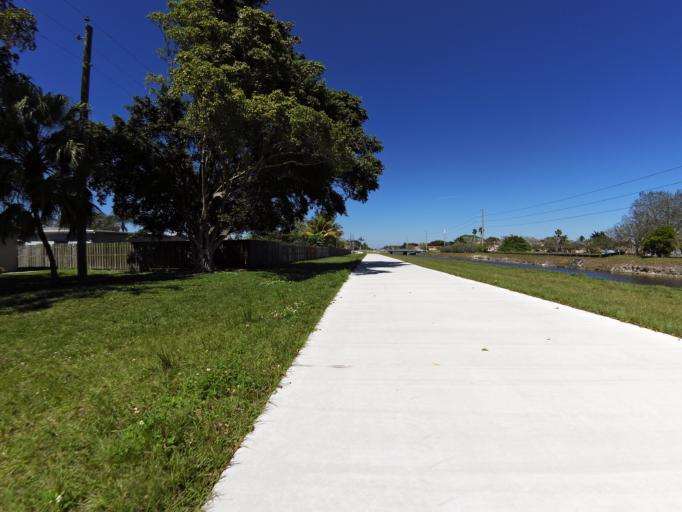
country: US
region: Florida
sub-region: Broward County
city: Tamarac
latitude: 26.1657
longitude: -80.2983
